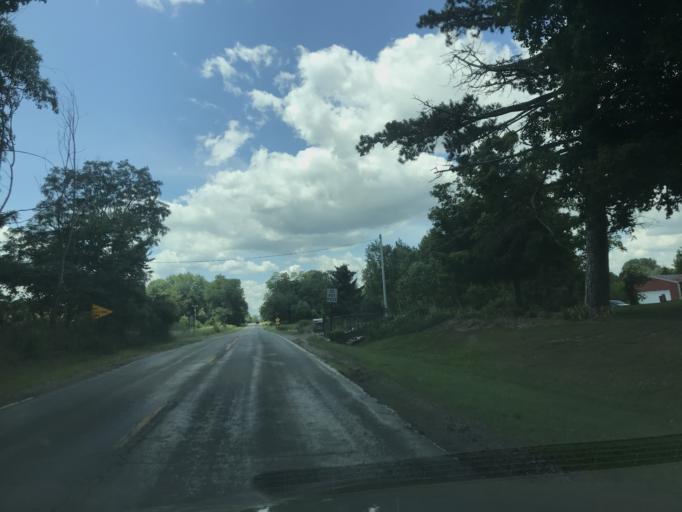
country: US
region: Michigan
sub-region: Ingham County
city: Leslie
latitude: 42.4511
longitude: -84.4980
